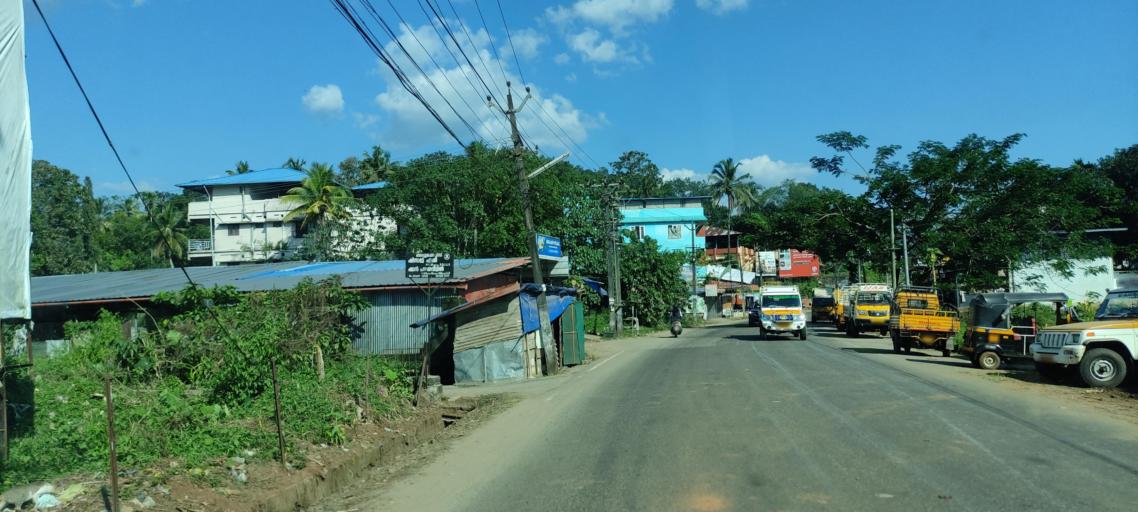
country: IN
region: Kerala
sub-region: Pattanamtitta
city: Pathanamthitta
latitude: 9.2683
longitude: 76.7994
